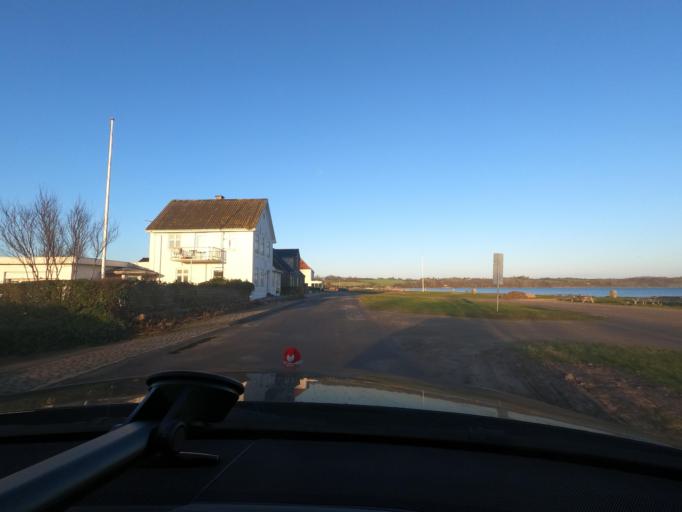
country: DK
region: South Denmark
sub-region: Sonderborg Kommune
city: Broager
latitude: 54.8955
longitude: 9.7005
